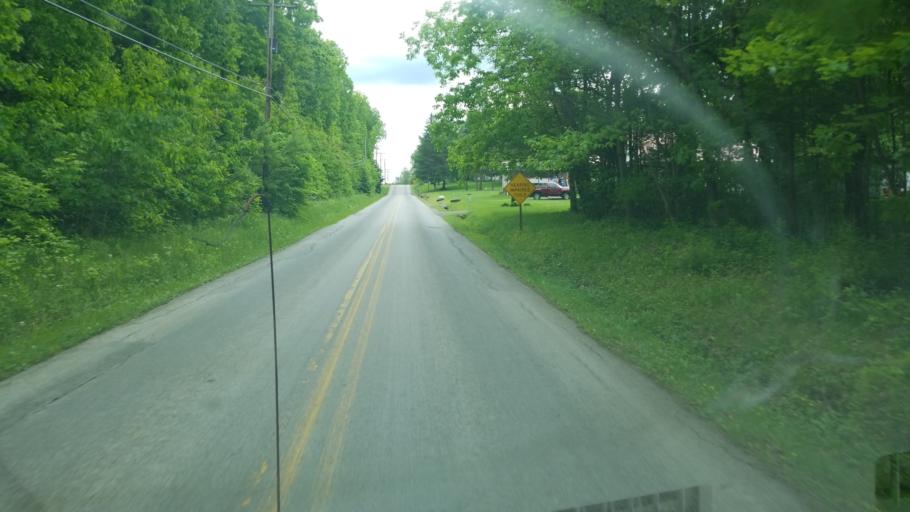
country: US
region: Pennsylvania
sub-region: Venango County
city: Franklin
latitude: 41.2041
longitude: -79.8444
